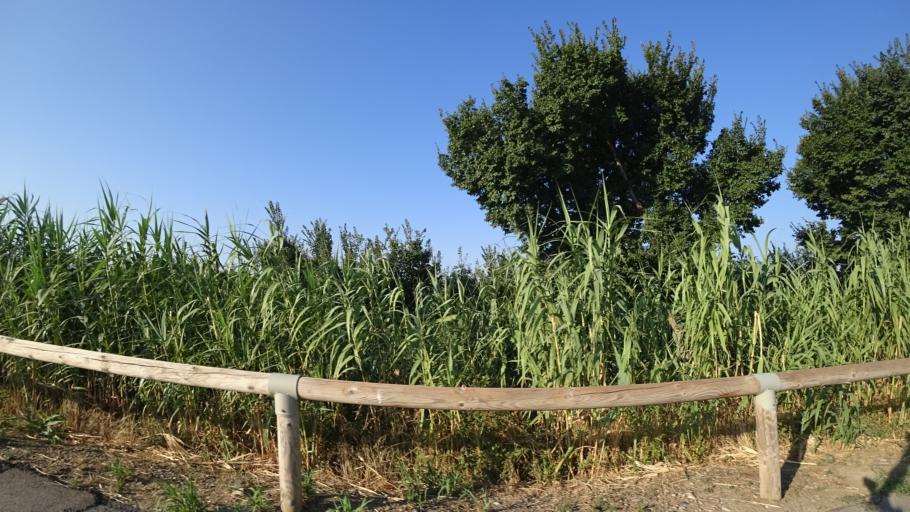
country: FR
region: Languedoc-Roussillon
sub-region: Departement des Pyrenees-Orientales
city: Pia
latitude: 42.7710
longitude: 2.9079
